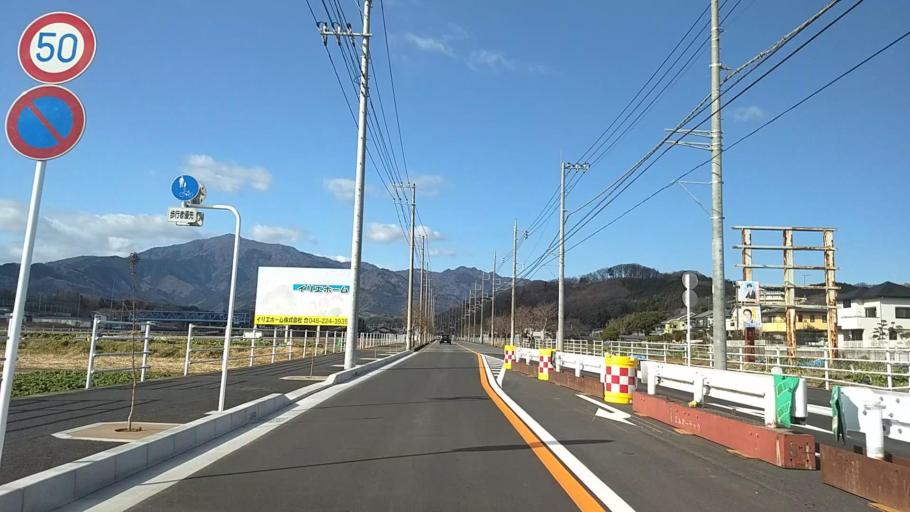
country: JP
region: Kanagawa
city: Atsugi
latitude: 35.4318
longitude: 139.3272
